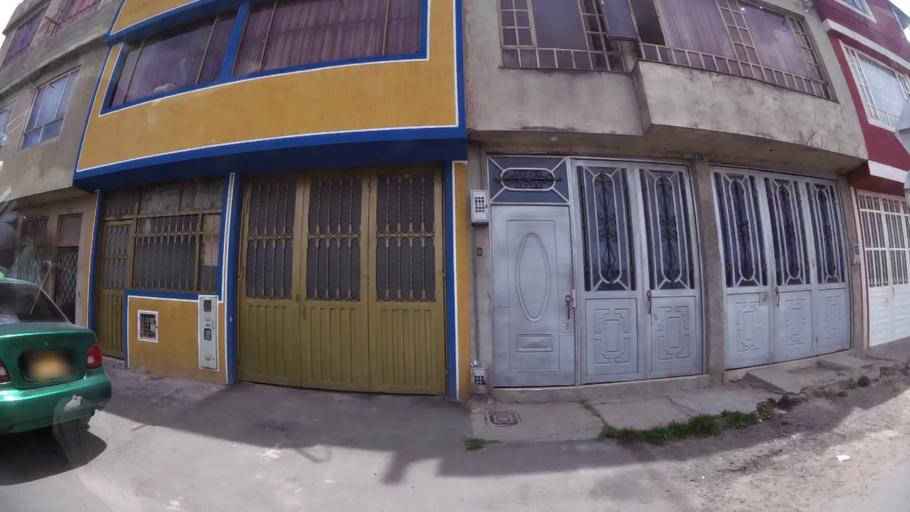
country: CO
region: Bogota D.C.
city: Bogota
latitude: 4.6504
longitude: -74.1412
